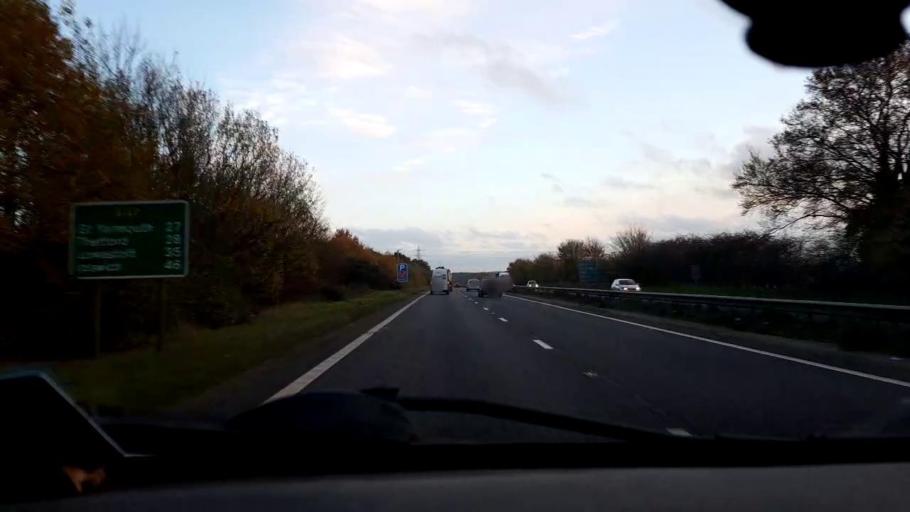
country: GB
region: England
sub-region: Norfolk
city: Costessey
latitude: 52.6454
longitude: 1.1901
